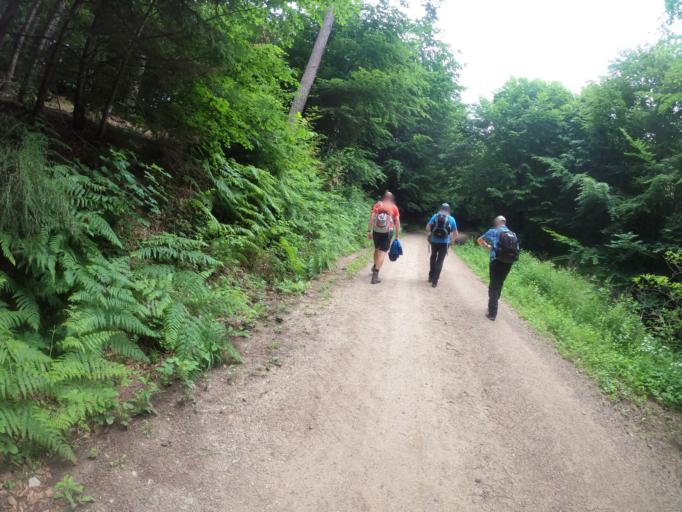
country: DE
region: Bavaria
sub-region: Upper Franconia
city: Litzendorf
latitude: 49.9273
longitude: 11.0280
